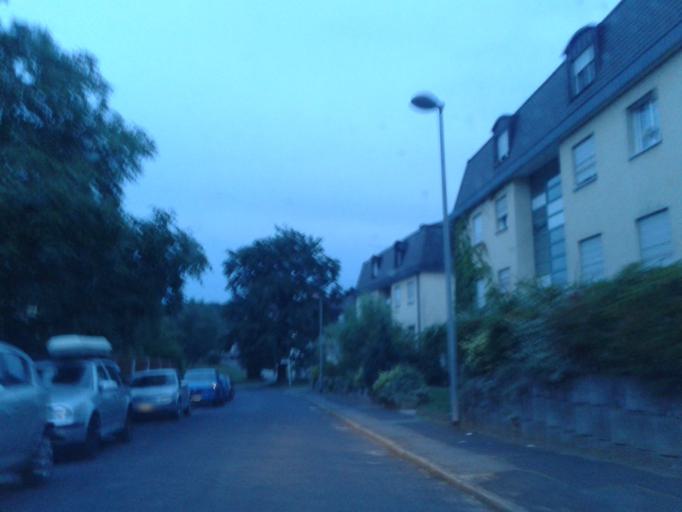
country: DE
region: Saxony
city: Radebeul
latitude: 51.1222
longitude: 13.6286
